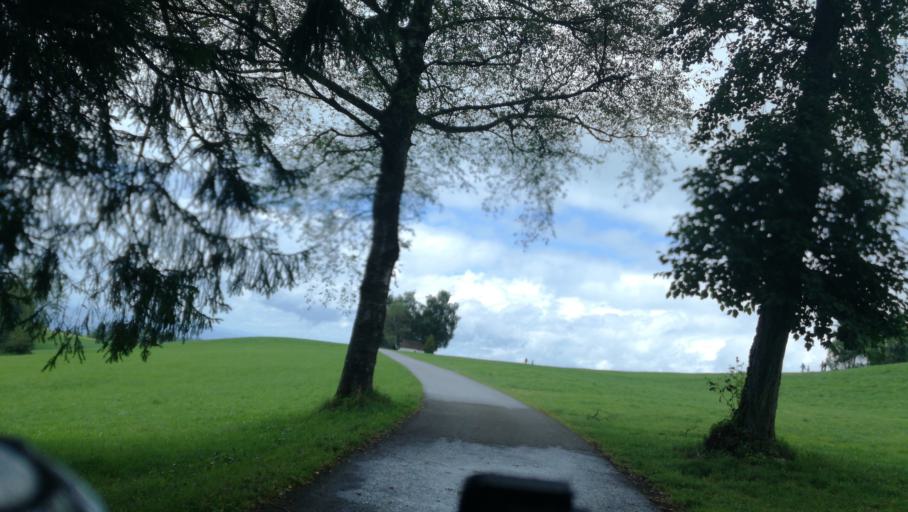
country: CH
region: Zug
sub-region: Zug
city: Walchwil
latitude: 47.1107
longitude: 8.5459
